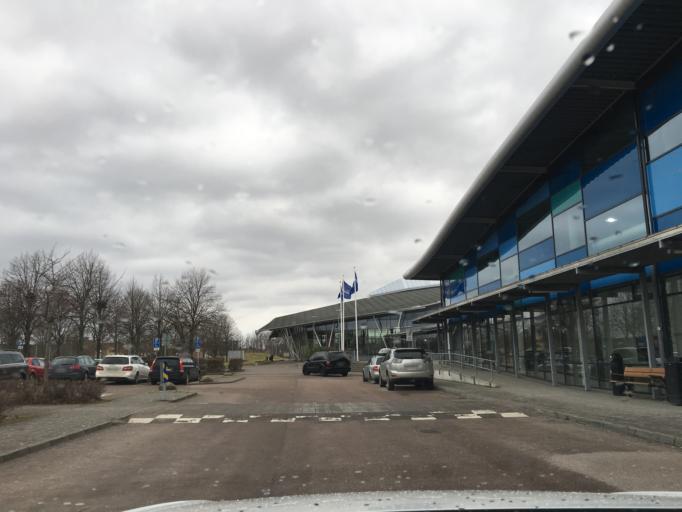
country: SE
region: Halland
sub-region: Halmstads Kommun
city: Halmstad
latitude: 56.6739
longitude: 12.8873
